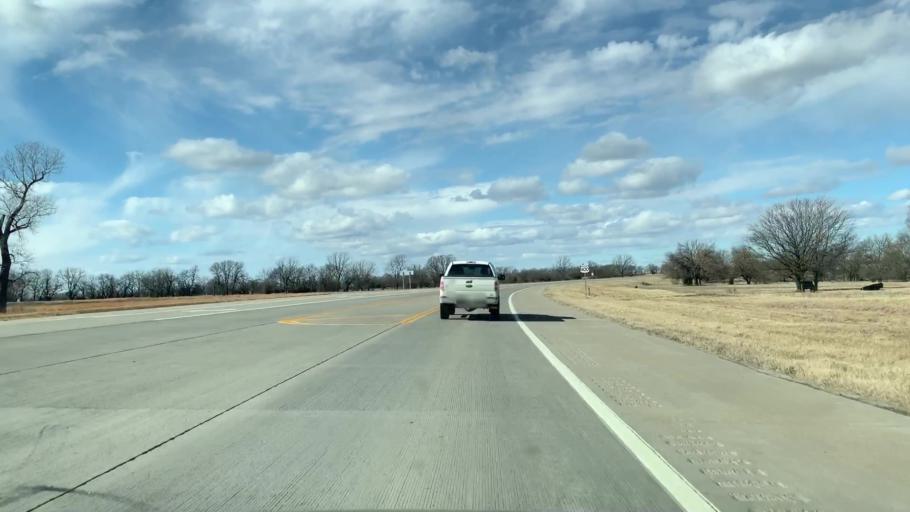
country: US
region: Kansas
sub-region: Labette County
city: Parsons
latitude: 37.3421
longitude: -95.1814
